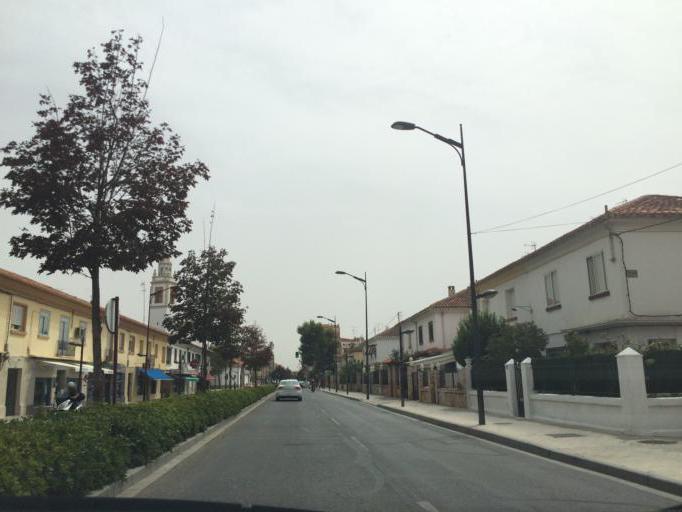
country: ES
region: Castille-La Mancha
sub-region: Provincia de Albacete
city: Albacete
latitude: 38.9933
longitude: -1.8706
